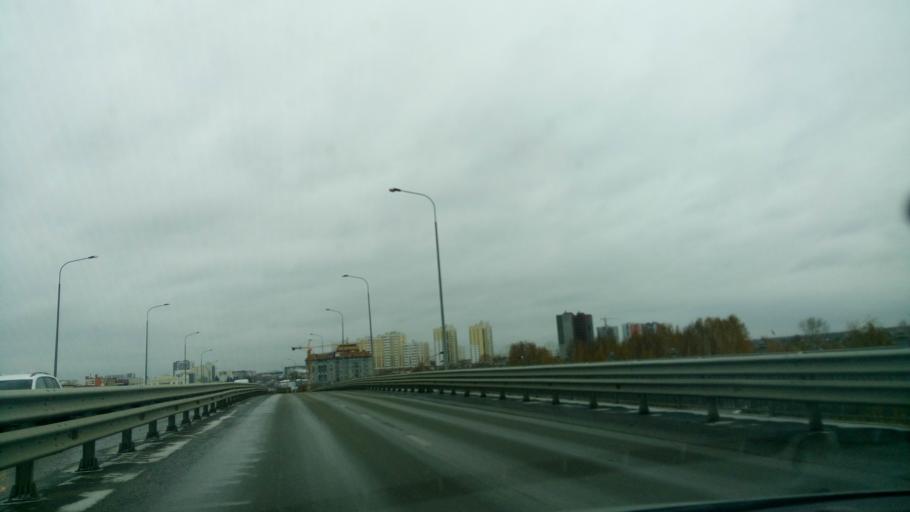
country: RU
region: Sverdlovsk
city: Verkhnyaya Pyshma
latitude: 56.9592
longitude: 60.5896
